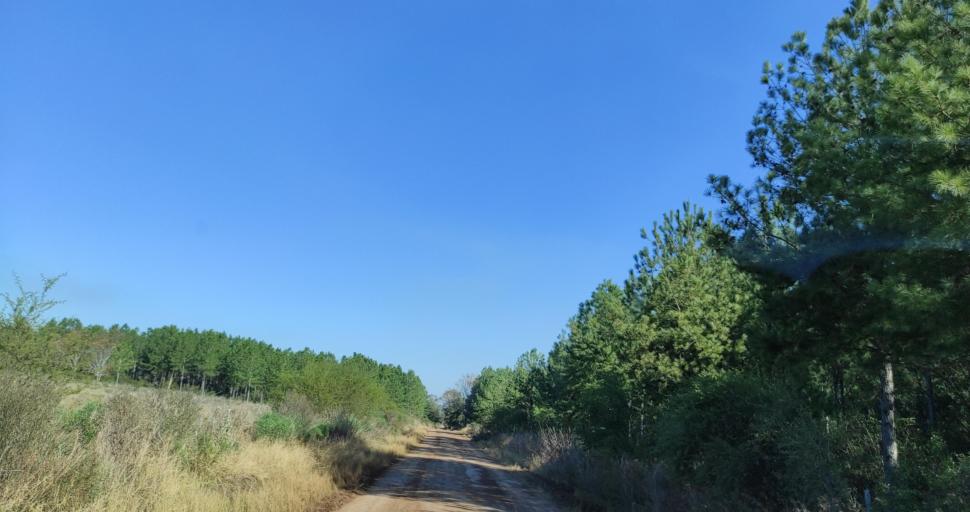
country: AR
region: Misiones
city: Cerro Cora
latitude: -27.6505
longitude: -55.6578
